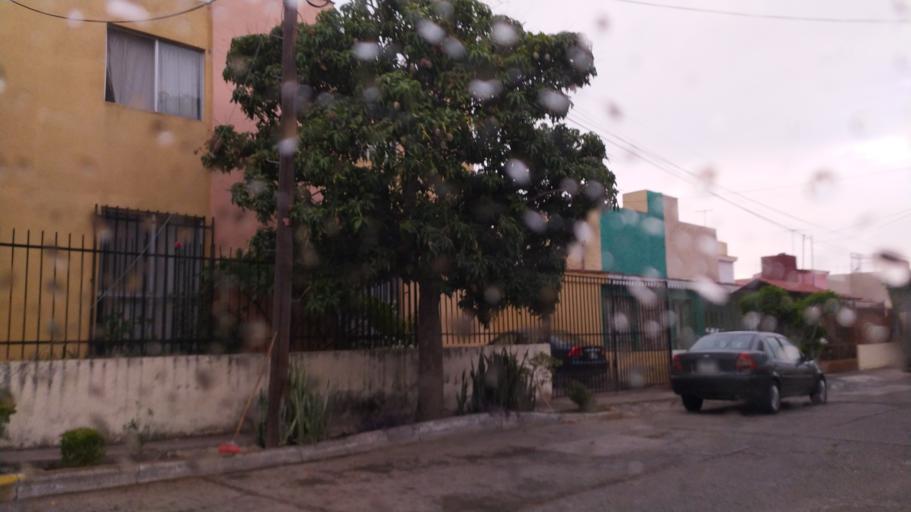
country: MX
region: Jalisco
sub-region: Zapopan
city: Zapopan
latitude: 20.7137
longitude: -103.3635
